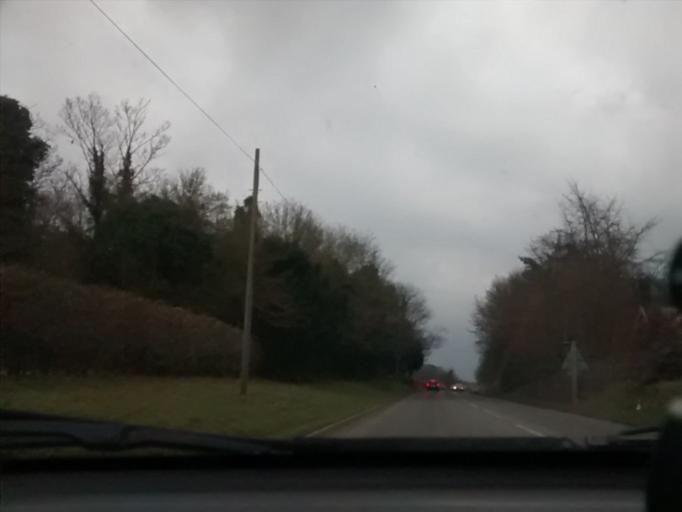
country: GB
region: England
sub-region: Cambridgeshire
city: Sawston
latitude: 52.1391
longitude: 0.2044
